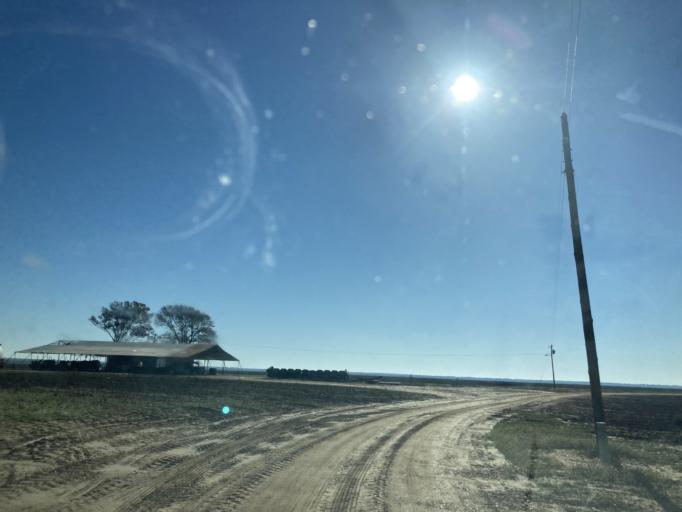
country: US
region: Mississippi
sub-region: Sharkey County
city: Rolling Fork
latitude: 32.8690
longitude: -90.6929
